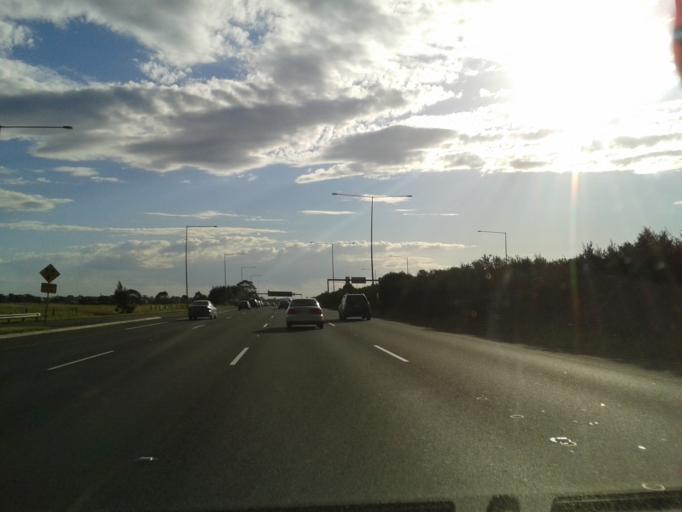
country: AU
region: Victoria
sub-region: Wyndham
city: Williams Landing
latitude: -37.8742
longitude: 144.7346
